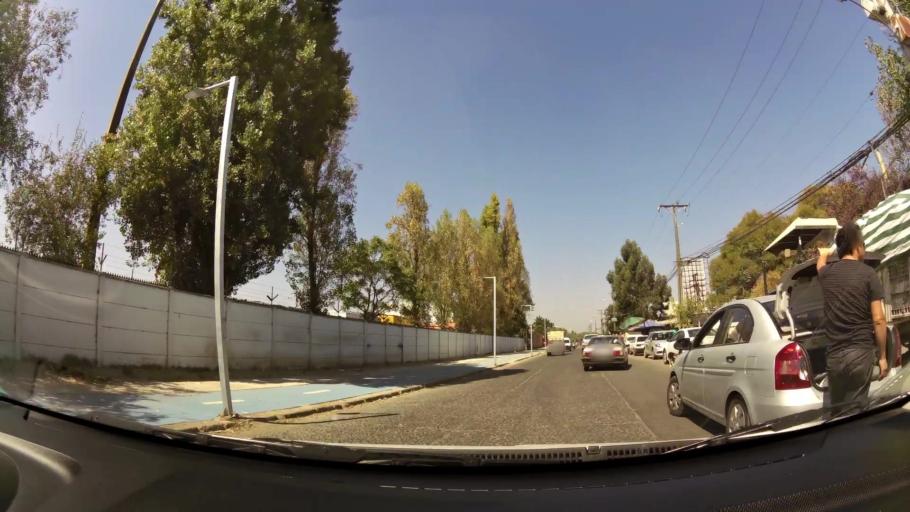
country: CL
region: Maule
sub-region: Provincia de Talca
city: Talca
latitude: -35.4213
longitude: -71.6363
